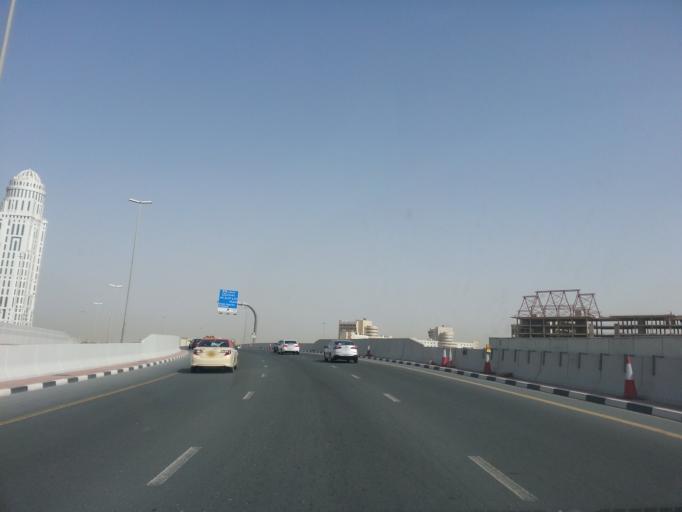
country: AE
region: Dubai
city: Dubai
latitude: 25.0642
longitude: 55.1320
